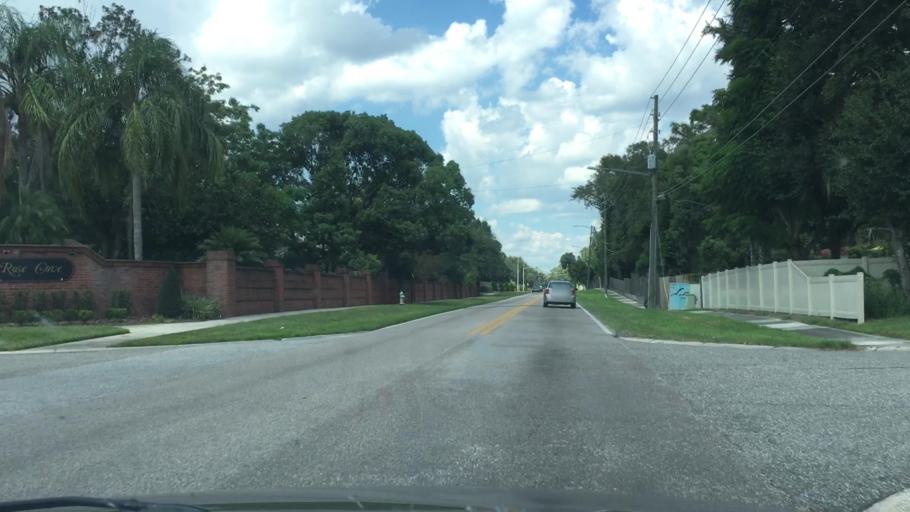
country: US
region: Florida
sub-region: Orange County
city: Lockhart
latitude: 28.6351
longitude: -81.4436
